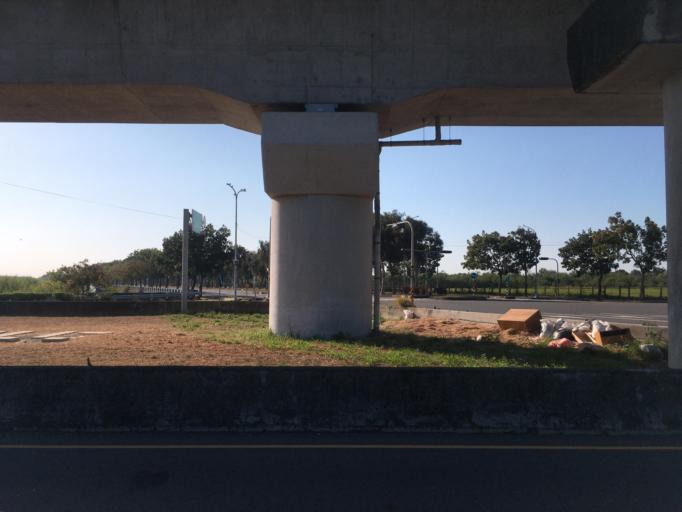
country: TW
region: Taiwan
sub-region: Chiayi
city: Taibao
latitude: 23.4520
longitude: 120.3237
